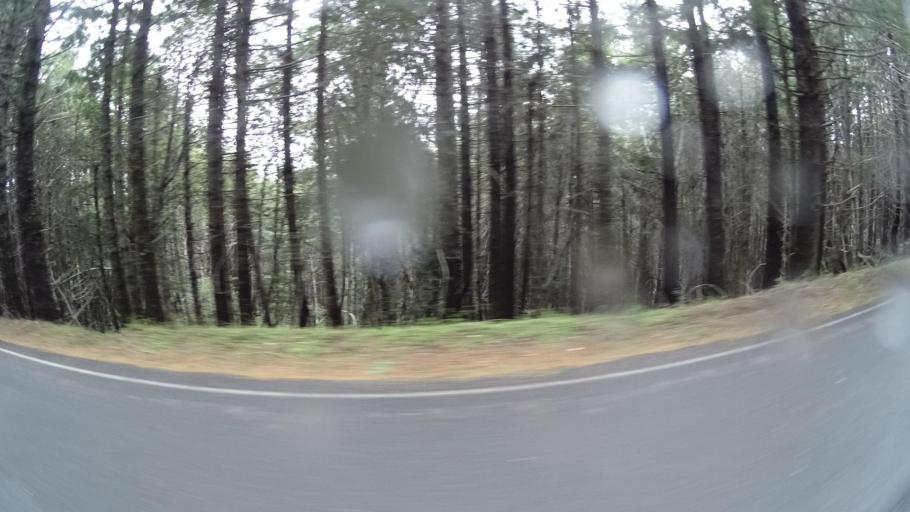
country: US
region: California
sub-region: Humboldt County
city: Willow Creek
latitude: 41.1593
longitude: -123.8178
